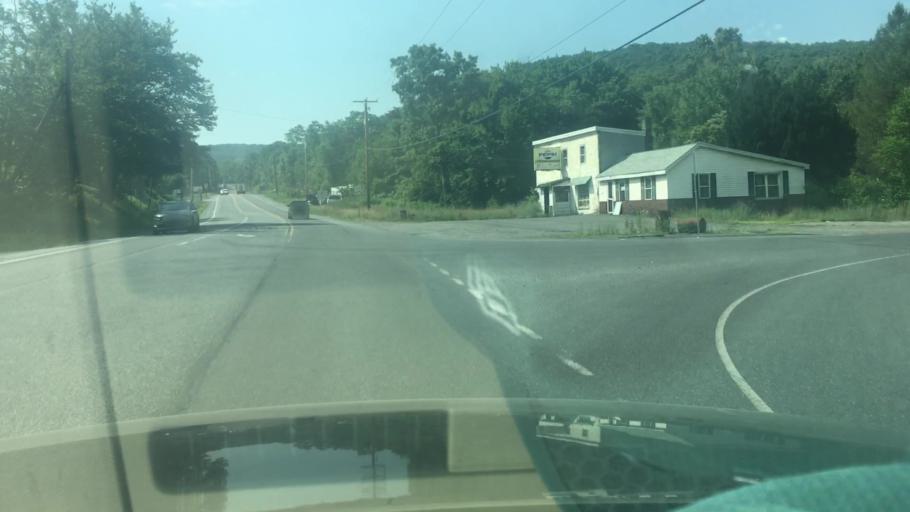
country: US
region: Pennsylvania
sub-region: Northumberland County
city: Kulpmont
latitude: 40.7810
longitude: -76.4471
